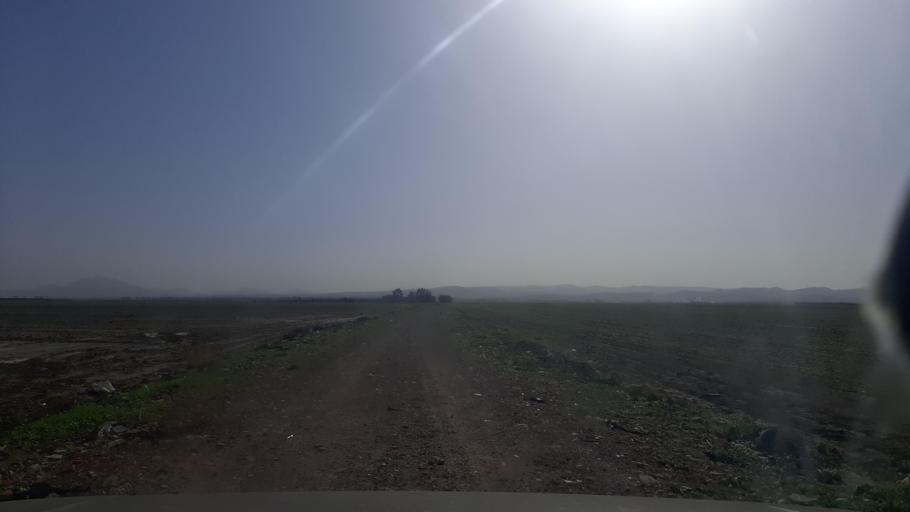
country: TN
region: Tunis
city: La Mohammedia
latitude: 36.6472
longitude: 10.0869
